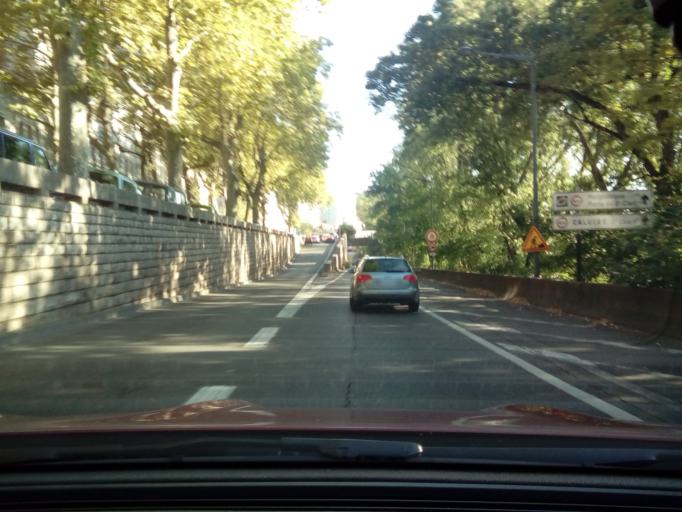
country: FR
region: Rhone-Alpes
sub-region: Departement du Rhone
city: Lyon
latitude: 45.7633
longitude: 4.8328
